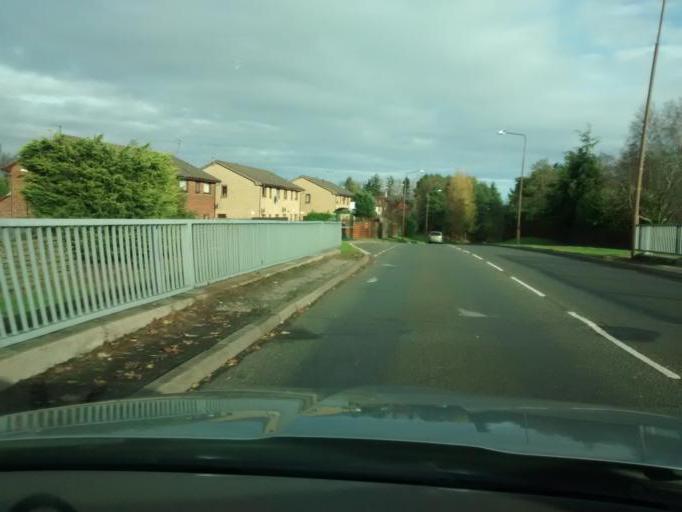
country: GB
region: Scotland
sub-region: West Lothian
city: Livingston
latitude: 55.8874
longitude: -3.5372
